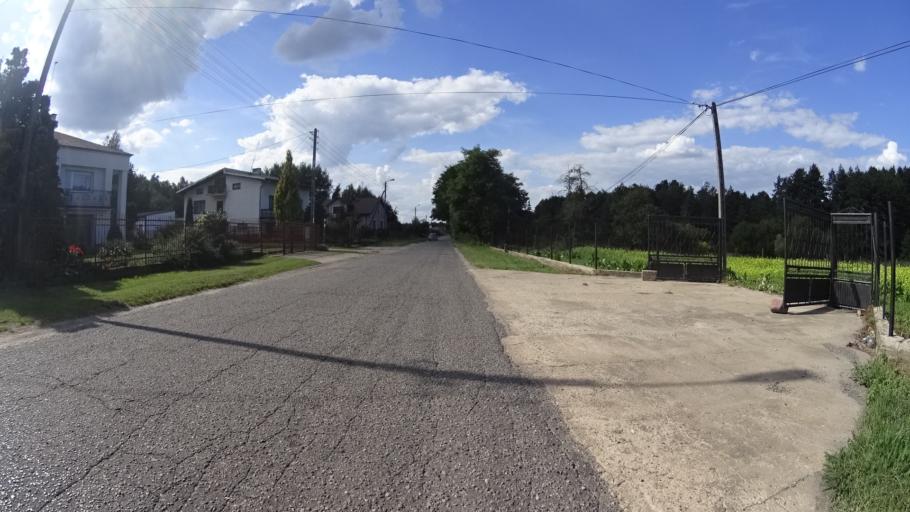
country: PL
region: Masovian Voivodeship
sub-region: Powiat grojecki
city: Mogielnica
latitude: 51.7011
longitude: 20.7104
